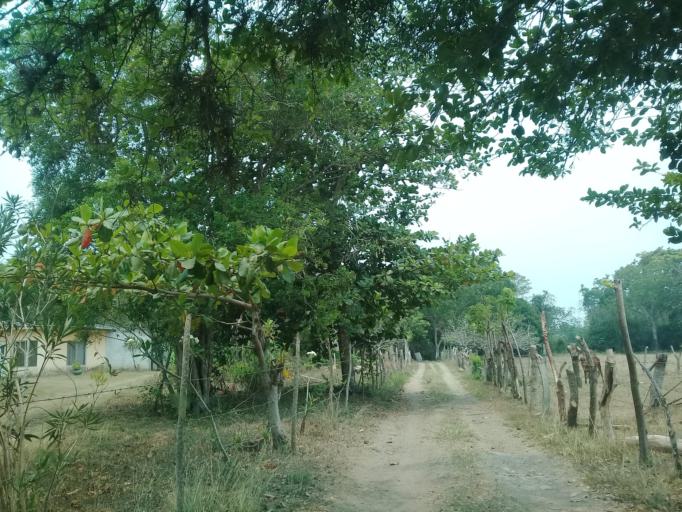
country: MX
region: Veracruz
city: Jamapa
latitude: 18.9586
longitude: -96.1962
